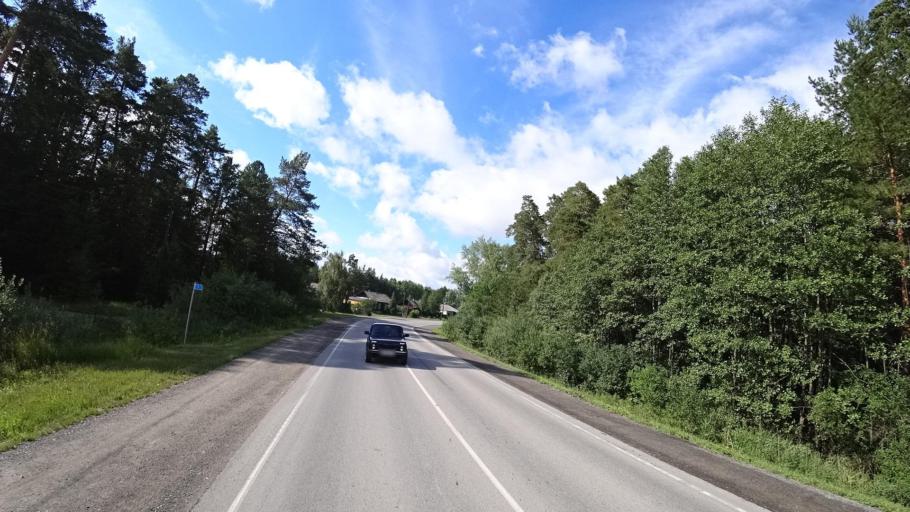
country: RU
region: Sverdlovsk
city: Kamyshlov
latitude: 56.8296
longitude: 62.6957
